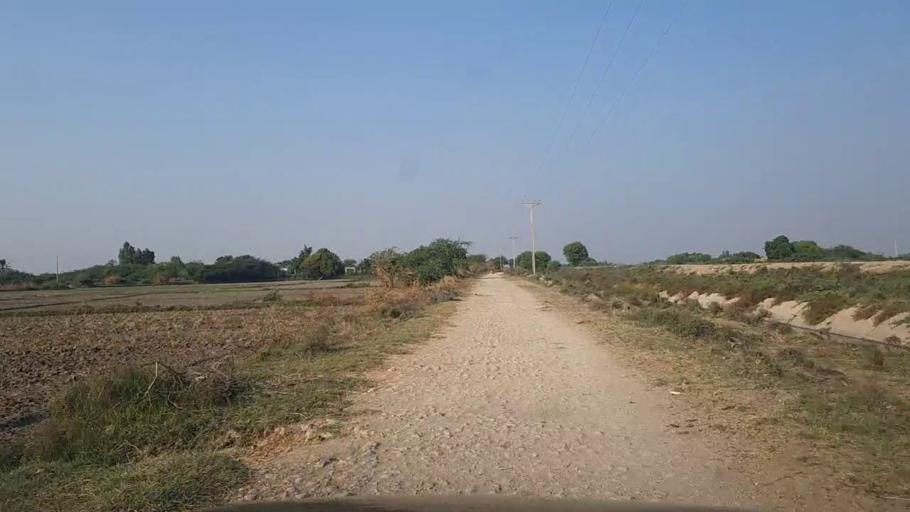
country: PK
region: Sindh
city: Thatta
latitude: 24.7534
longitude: 67.9593
